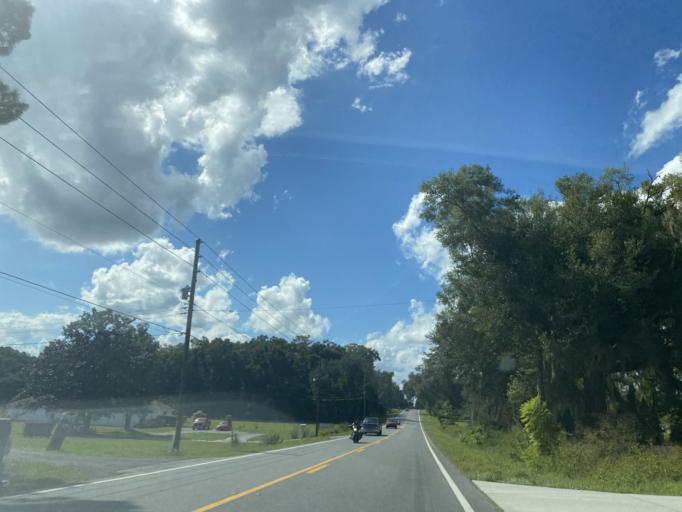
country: US
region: Florida
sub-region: Sumter County
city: The Villages
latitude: 28.9820
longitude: -81.9646
